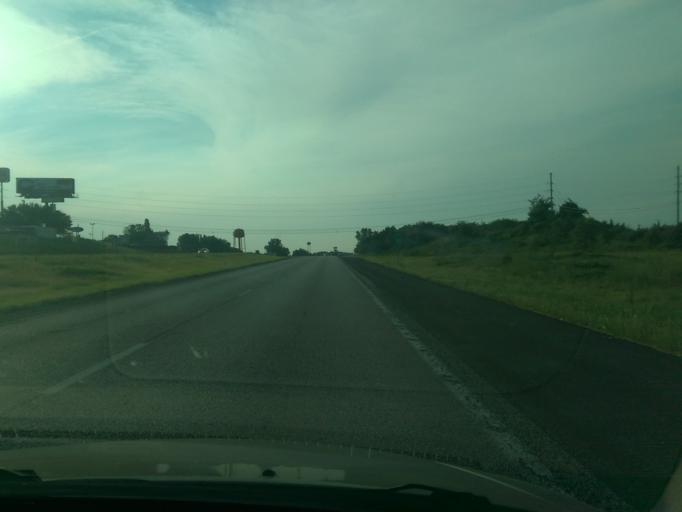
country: US
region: Missouri
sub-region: Platte County
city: Platte City
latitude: 39.3544
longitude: -94.7626
